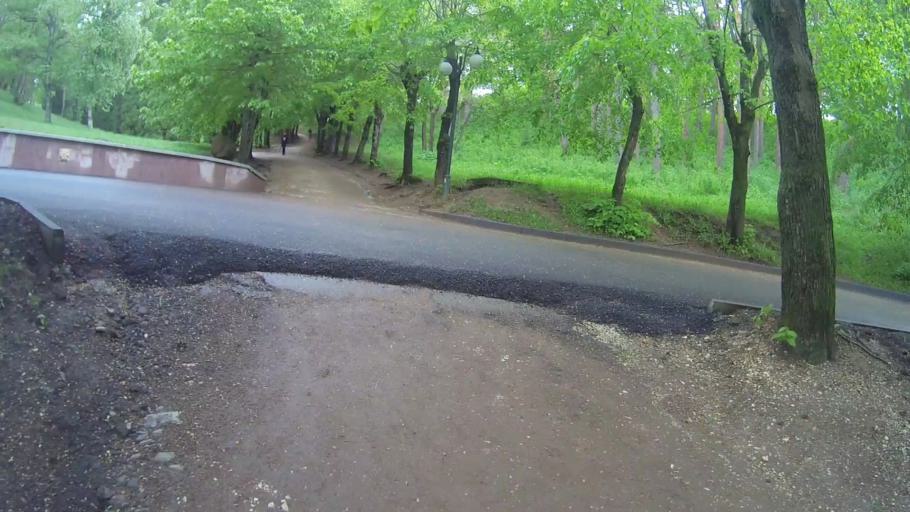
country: RU
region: Stavropol'skiy
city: Kislovodsk
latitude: 43.8969
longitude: 42.7287
